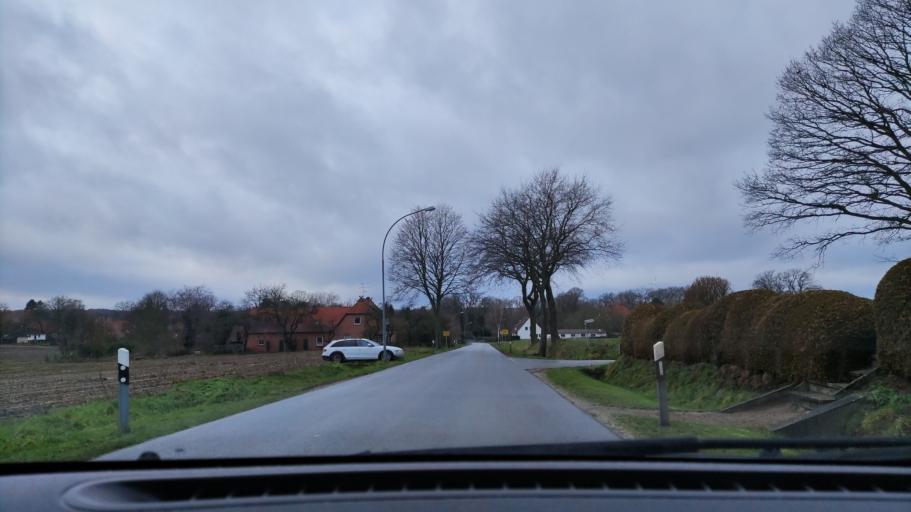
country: DE
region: Lower Saxony
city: Natendorf
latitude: 53.0802
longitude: 10.4781
